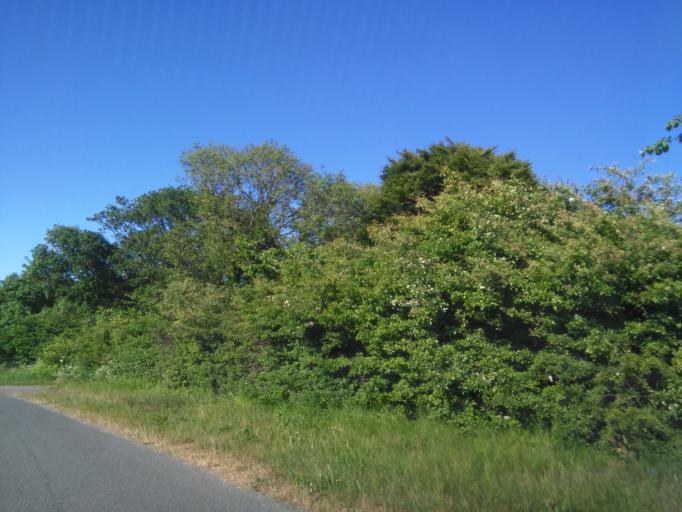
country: DK
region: Capital Region
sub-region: Bornholm Kommune
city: Ronne
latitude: 55.2758
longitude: 14.7629
